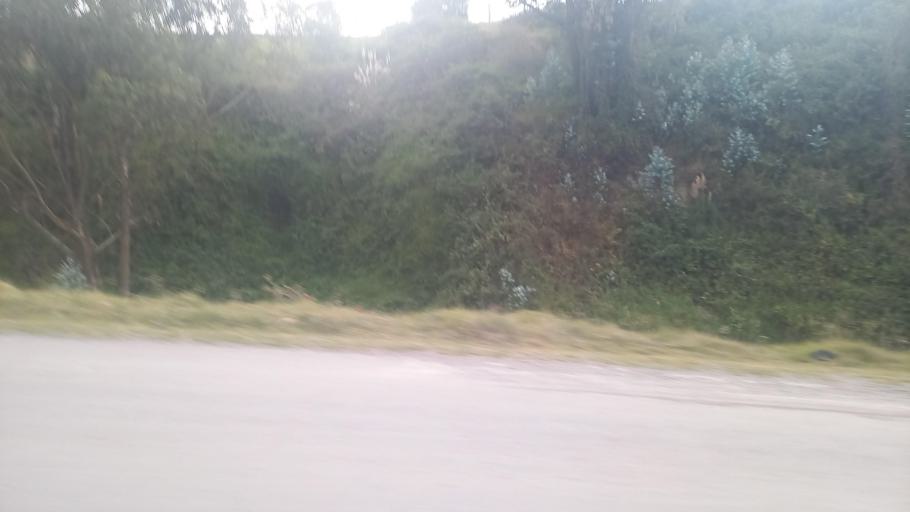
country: EC
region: Pichincha
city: Cayambe
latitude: 0.0719
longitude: -78.1072
